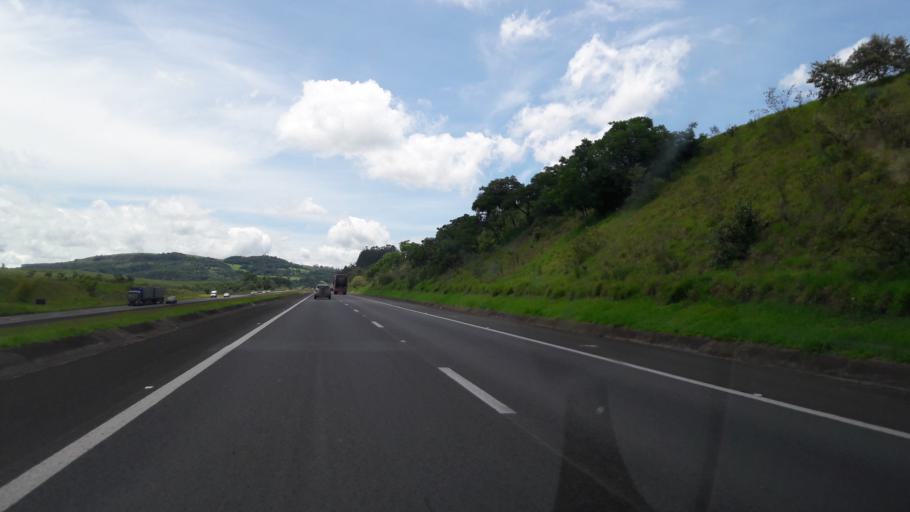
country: BR
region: Sao Paulo
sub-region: Itatinga
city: Itatinga
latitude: -23.1256
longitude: -48.4760
